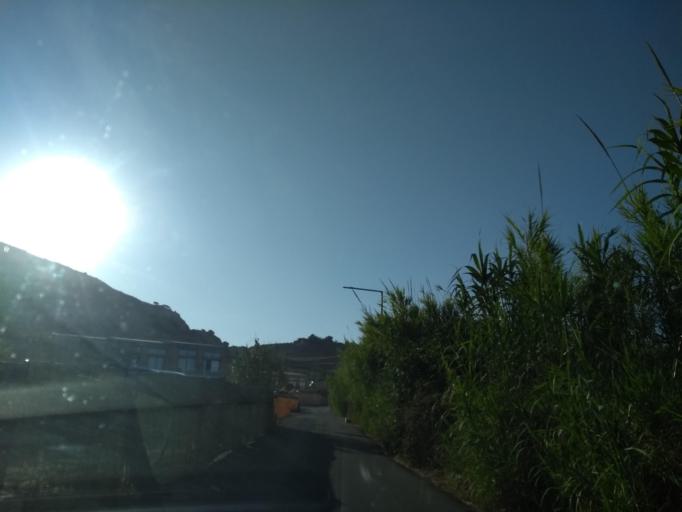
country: GR
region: Crete
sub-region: Nomos Chanias
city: Kalivai
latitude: 35.4647
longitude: 24.1564
